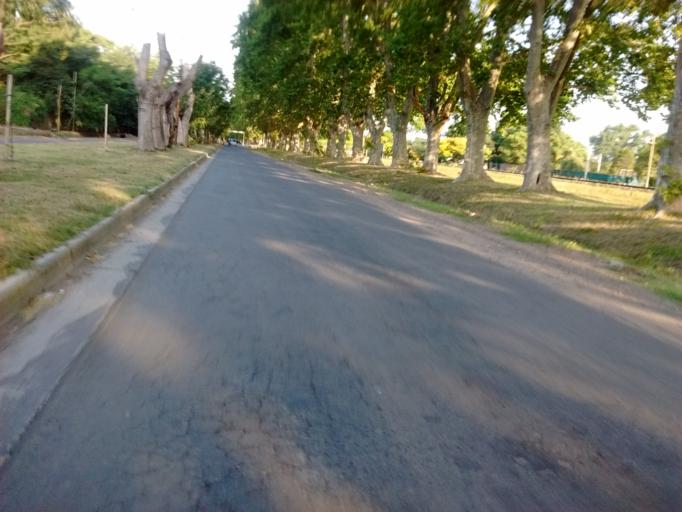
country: AR
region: Santa Fe
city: Funes
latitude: -32.9184
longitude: -60.8015
